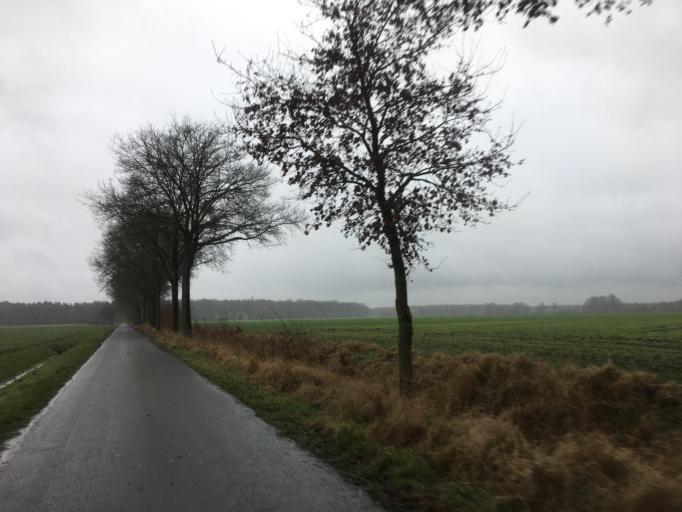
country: DE
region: North Rhine-Westphalia
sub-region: Regierungsbezirk Munster
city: Senden
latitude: 51.9004
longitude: 7.5328
